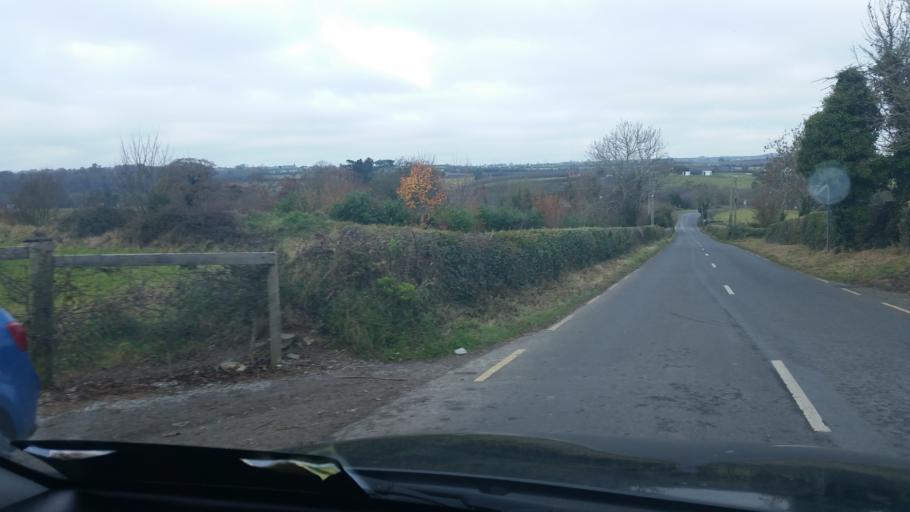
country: IE
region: Leinster
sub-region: Lu
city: Tullyallen
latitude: 53.7176
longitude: -6.4103
